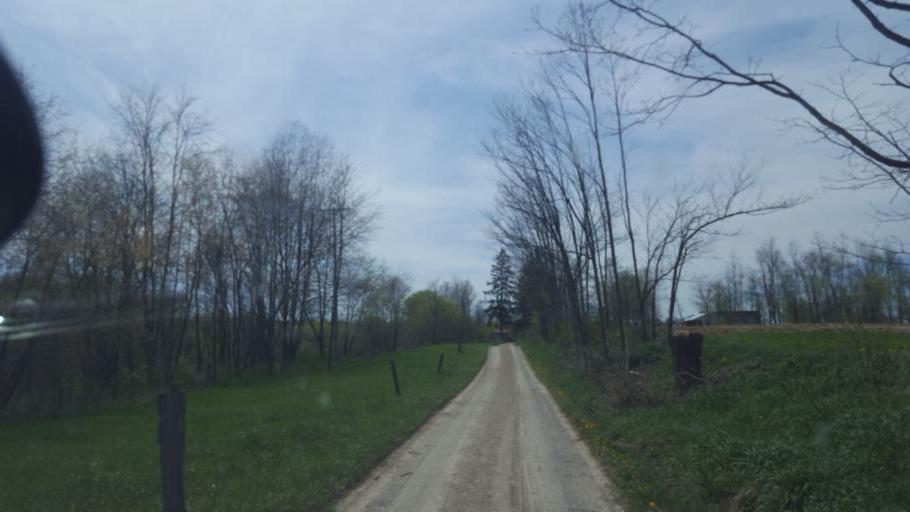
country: US
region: Ohio
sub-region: Ashland County
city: Ashland
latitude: 40.9110
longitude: -82.3595
